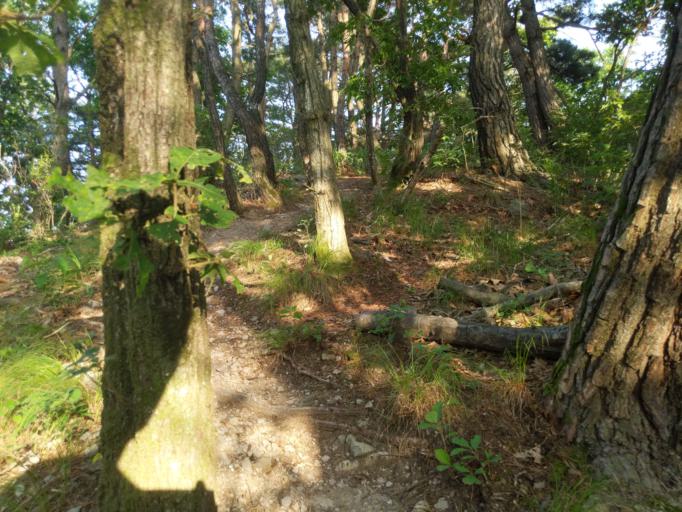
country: KR
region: Daegu
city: Hwawon
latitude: 35.7827
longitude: 128.5471
